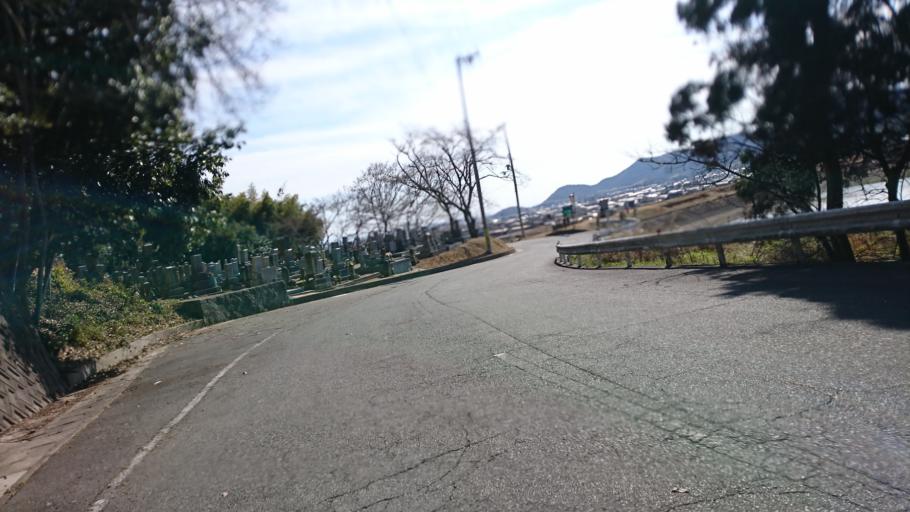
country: JP
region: Hyogo
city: Kakogawacho-honmachi
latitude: 34.8284
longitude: 134.8113
